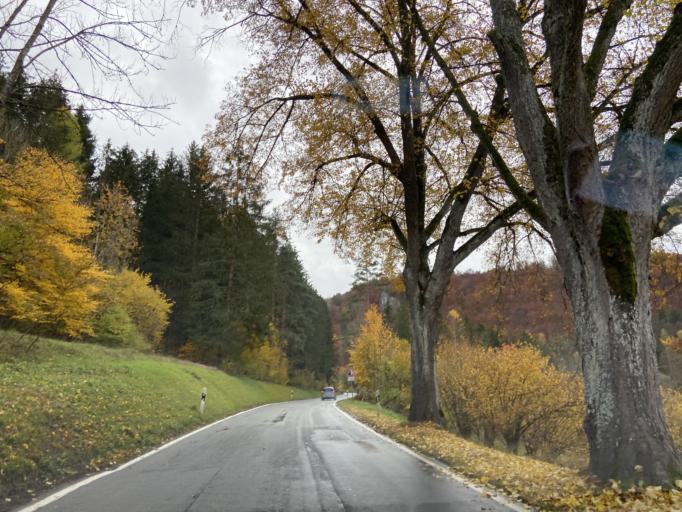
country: DE
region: Baden-Wuerttemberg
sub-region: Tuebingen Region
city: Leibertingen
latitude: 48.0771
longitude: 9.0346
